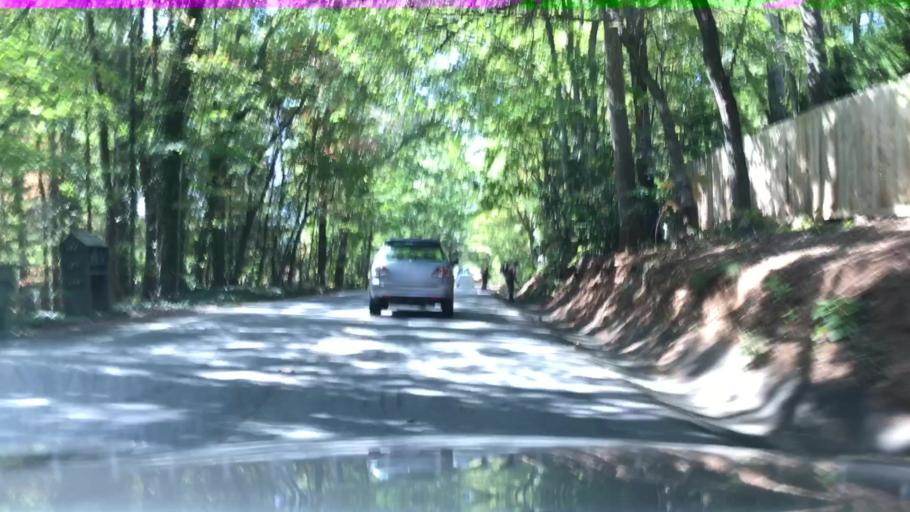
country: US
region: North Carolina
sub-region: Buncombe County
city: Royal Pines
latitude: 35.4956
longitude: -82.5323
